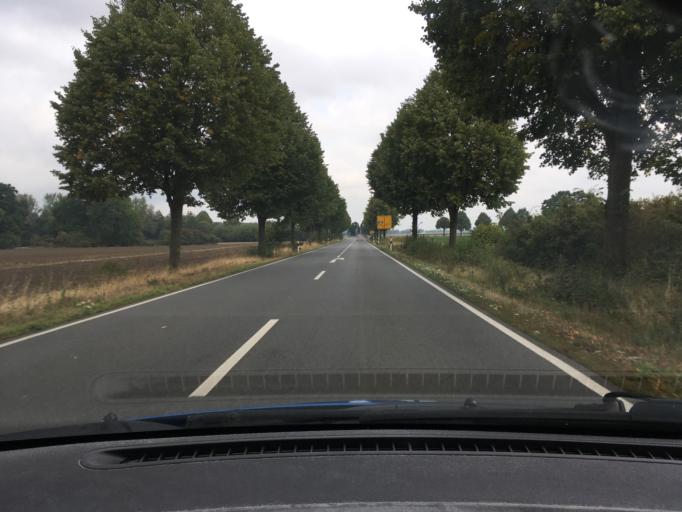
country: DE
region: Lower Saxony
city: Grossgoltern
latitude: 52.3300
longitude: 9.4687
